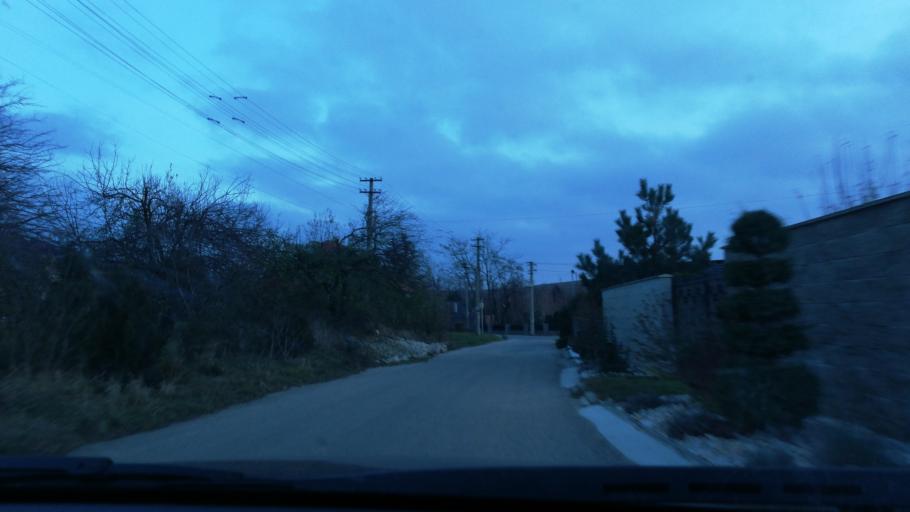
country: SK
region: Nitriansky
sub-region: Okres Nitra
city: Nitra
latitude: 48.3131
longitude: 17.9955
